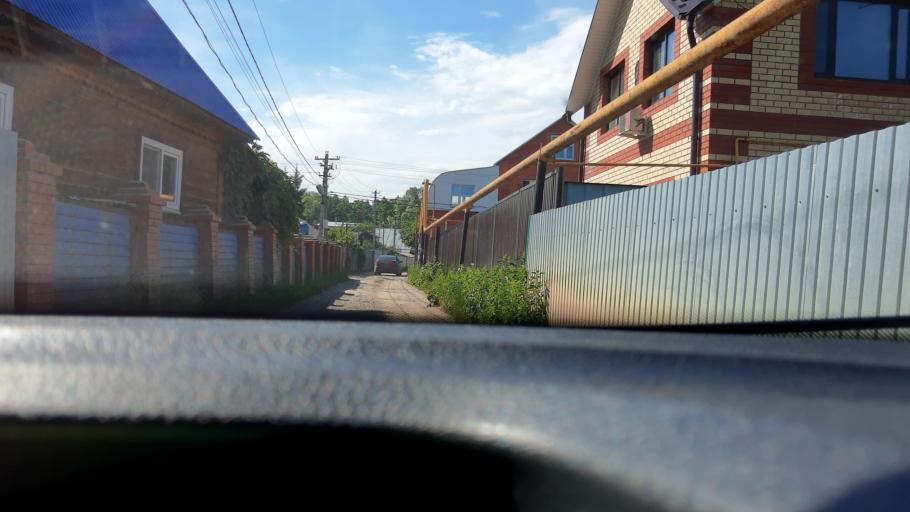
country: RU
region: Bashkortostan
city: Avdon
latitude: 54.6769
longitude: 55.8449
